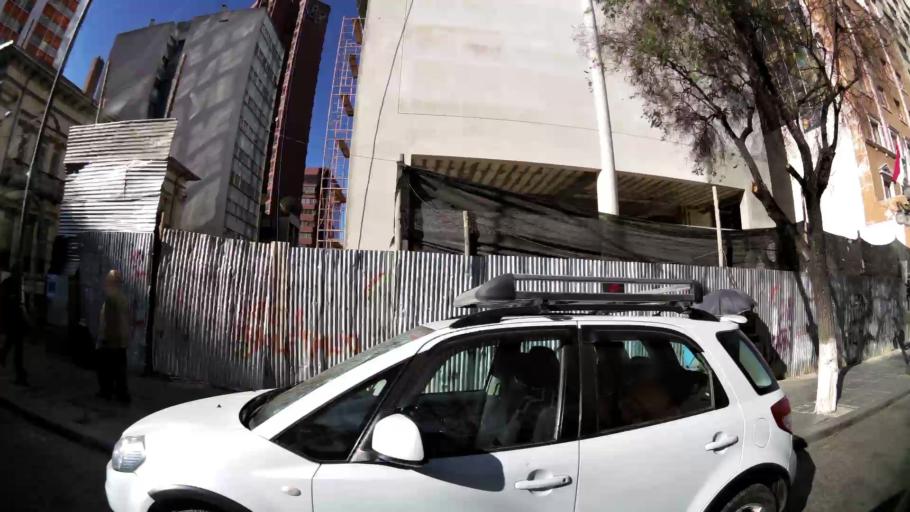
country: BO
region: La Paz
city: La Paz
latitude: -16.5028
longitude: -68.1319
